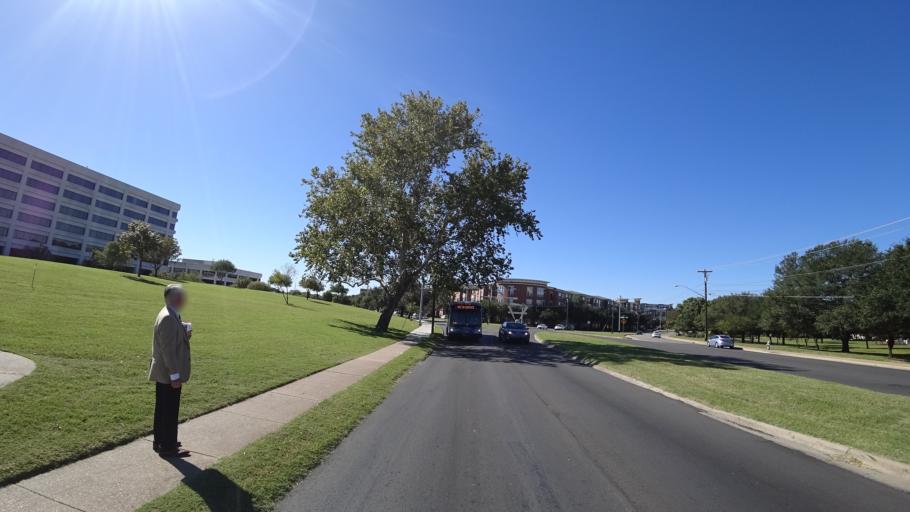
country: US
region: Texas
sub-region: Travis County
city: Austin
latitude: 30.3172
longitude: -97.7317
